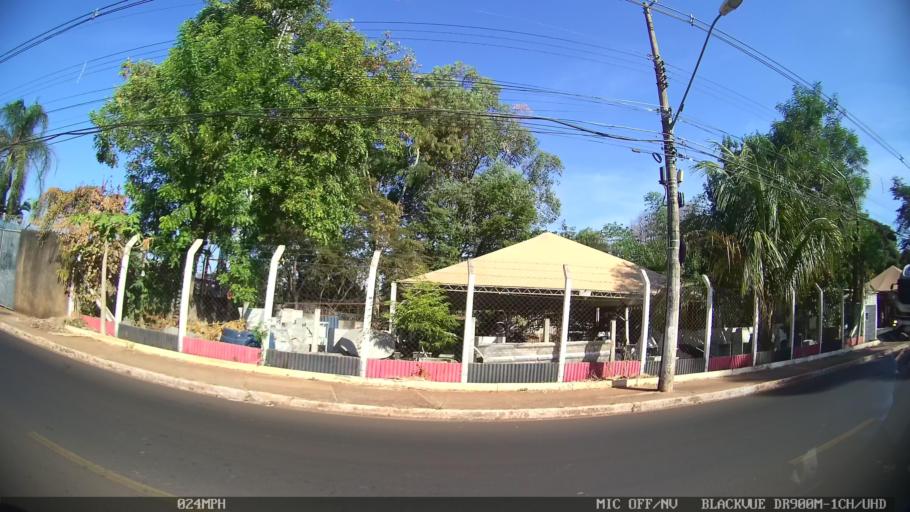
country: BR
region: Sao Paulo
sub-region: Ribeirao Preto
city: Ribeirao Preto
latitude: -21.1841
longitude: -47.7658
